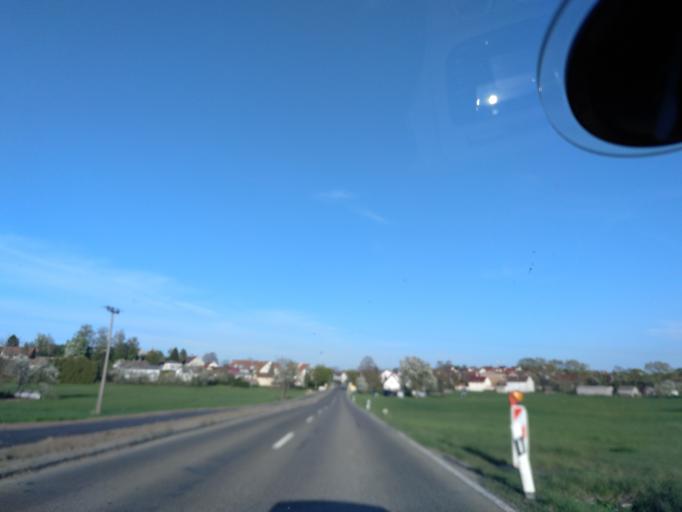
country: DE
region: Baden-Wuerttemberg
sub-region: Regierungsbezirk Stuttgart
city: Crailsheim
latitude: 49.1392
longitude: 10.0157
